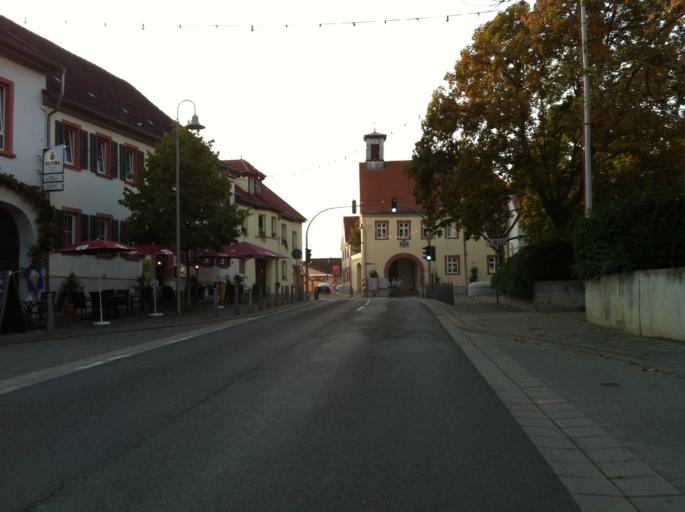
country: DE
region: Rheinland-Pfalz
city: Schwabenheim
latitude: 49.9315
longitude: 8.0970
